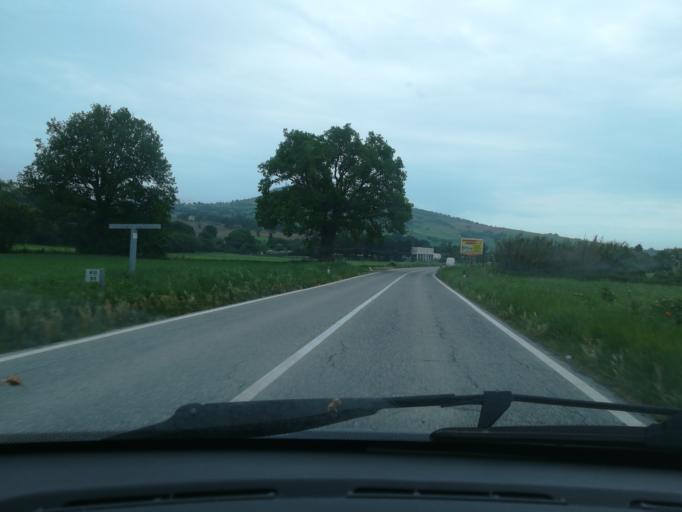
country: IT
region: The Marches
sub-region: Provincia di Macerata
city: San Severino Marche
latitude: 43.2533
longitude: 13.2315
